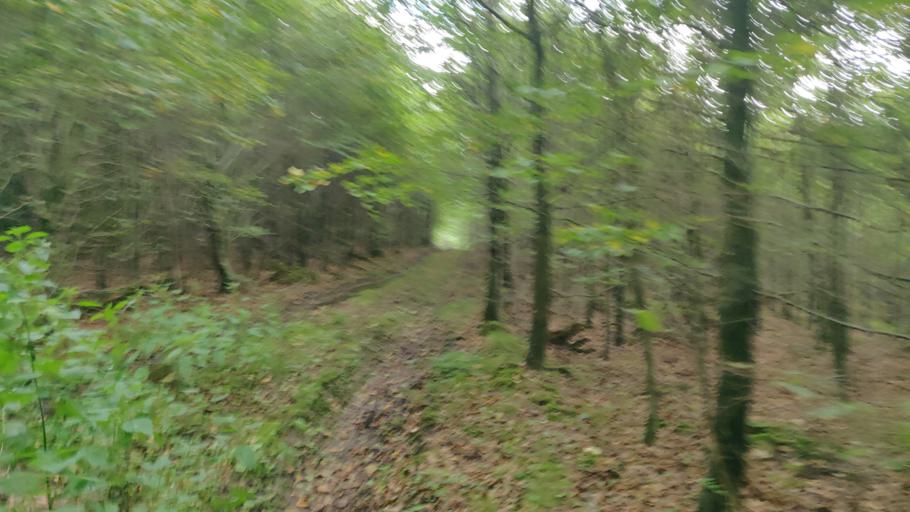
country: DK
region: South Denmark
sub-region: Kolding Kommune
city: Lunderskov
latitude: 55.5472
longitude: 9.3632
